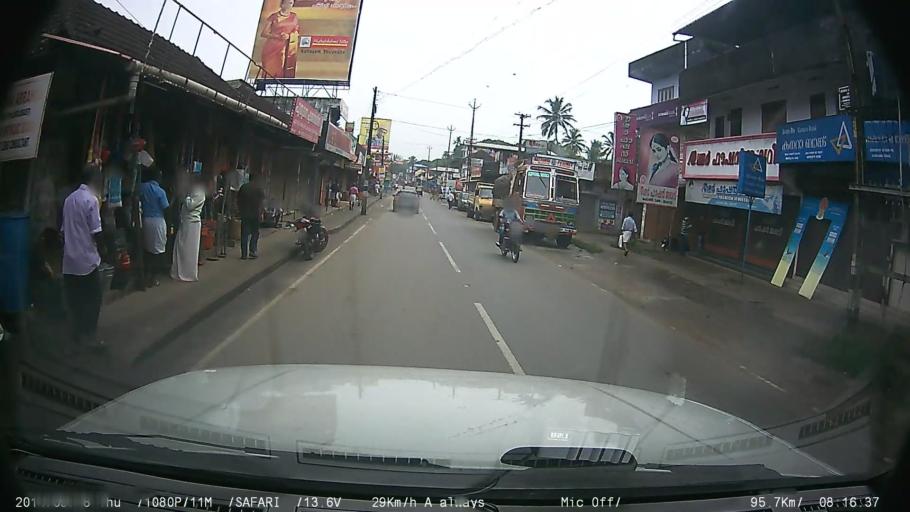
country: IN
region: Kerala
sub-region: Kottayam
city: Kottayam
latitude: 9.6362
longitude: 76.6063
